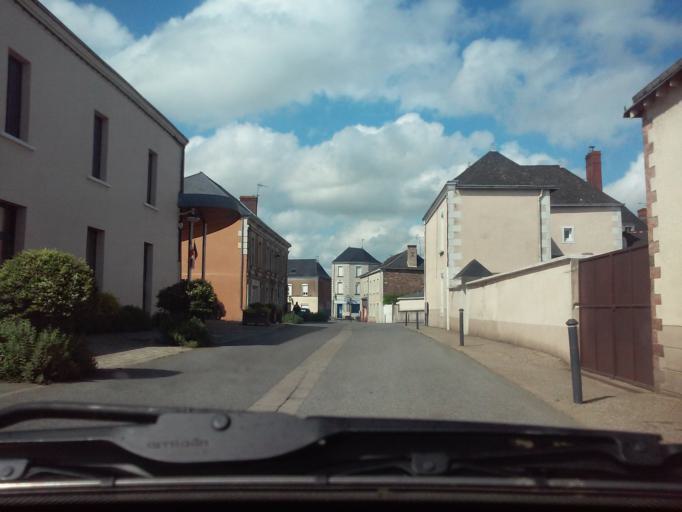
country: FR
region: Pays de la Loire
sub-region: Departement de la Mayenne
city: Quelaines-Saint-Gault
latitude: 47.9231
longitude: -0.8023
